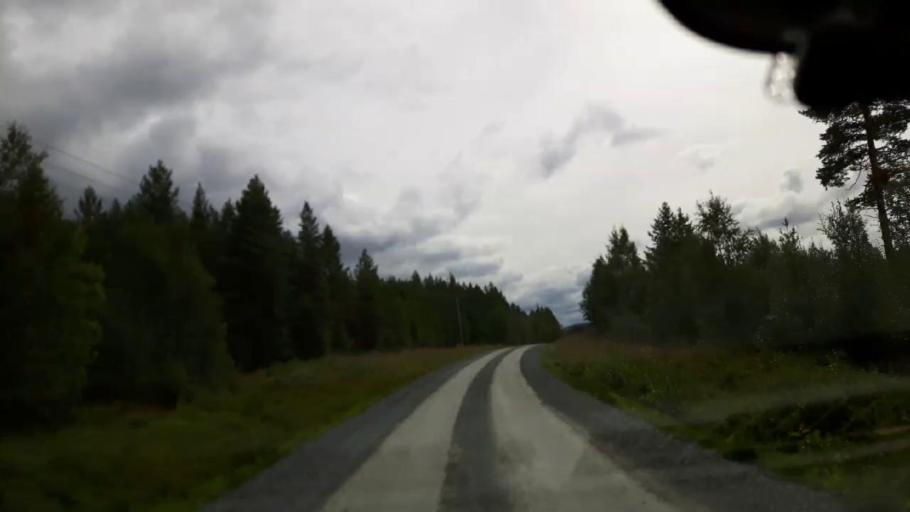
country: SE
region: Jaemtland
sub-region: Krokoms Kommun
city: Valla
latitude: 63.6014
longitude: 14.1353
